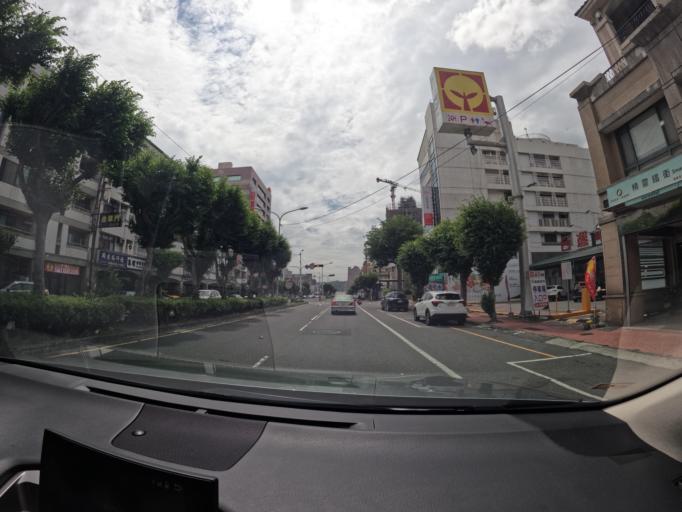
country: TW
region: Taiwan
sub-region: Changhua
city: Chang-hua
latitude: 24.0957
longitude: 120.5493
